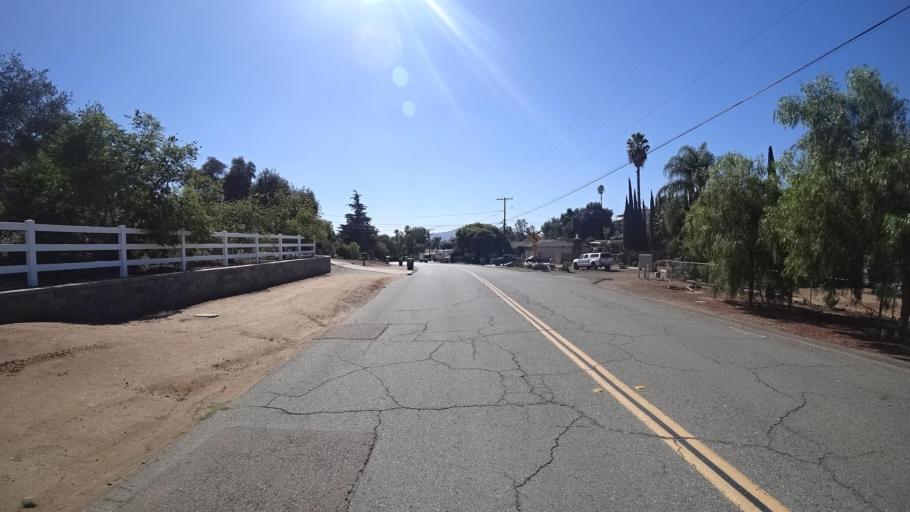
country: US
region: California
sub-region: San Diego County
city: Bostonia
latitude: 32.8171
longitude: -116.9303
